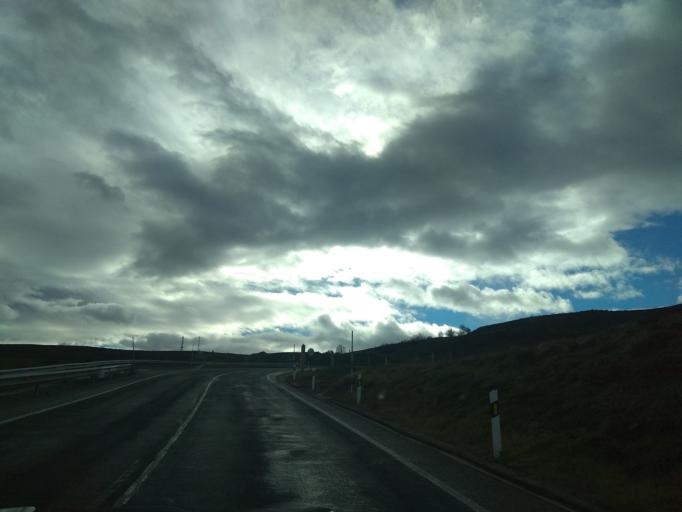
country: ES
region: Cantabria
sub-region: Provincia de Cantabria
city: San Pedro del Romeral
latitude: 43.0617
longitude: -3.8865
